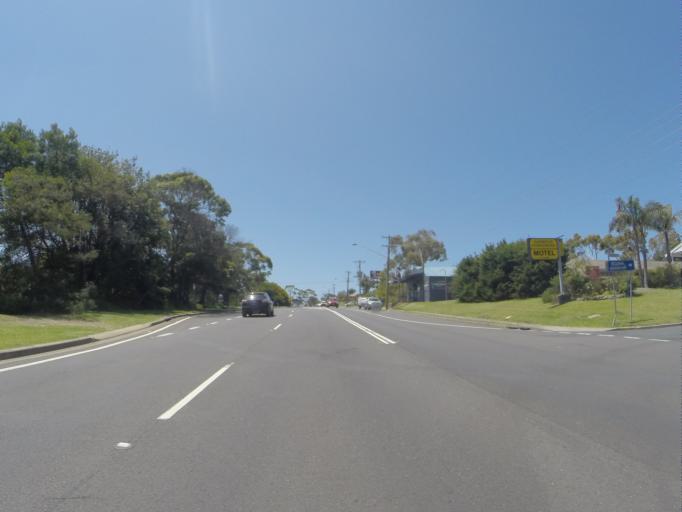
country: AU
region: New South Wales
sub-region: Shoalhaven Shire
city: Ulladulla
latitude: -35.3533
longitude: 150.4751
